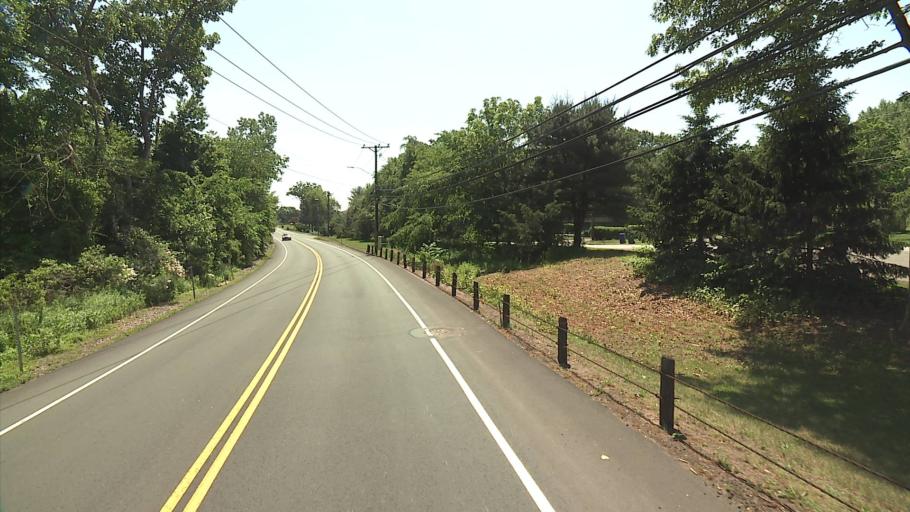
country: US
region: Connecticut
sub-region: Hartford County
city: Manchester
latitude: 41.8157
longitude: -72.5330
